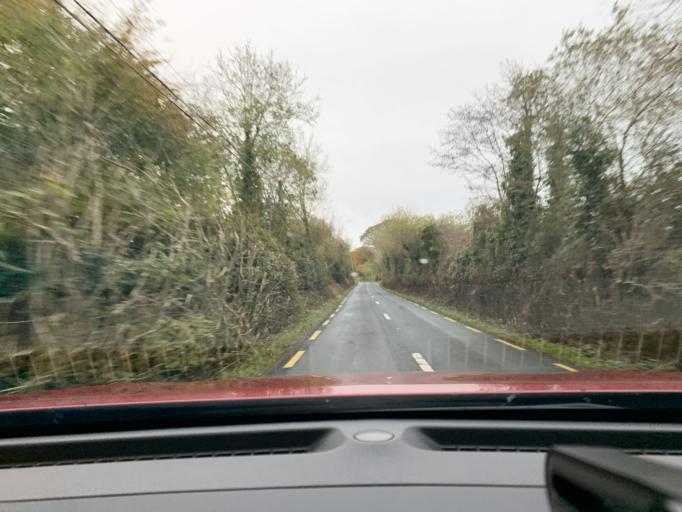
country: IE
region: Connaught
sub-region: Roscommon
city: Ballaghaderreen
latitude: 53.9748
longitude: -8.5366
